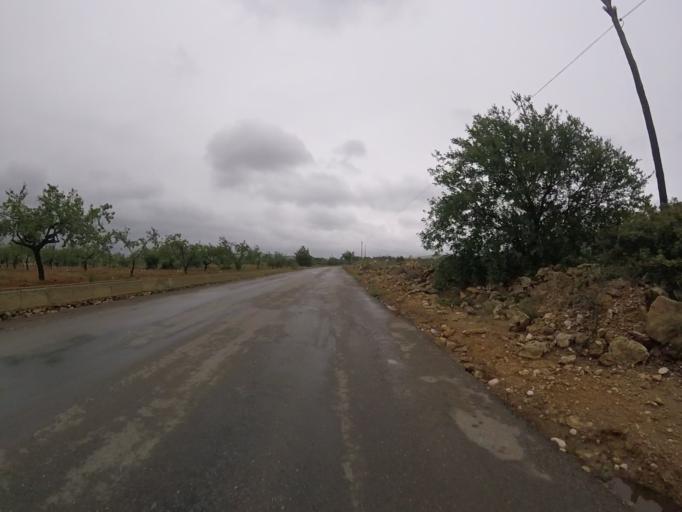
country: ES
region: Valencia
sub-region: Provincia de Castello
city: Alcoceber
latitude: 40.2453
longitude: 0.2474
